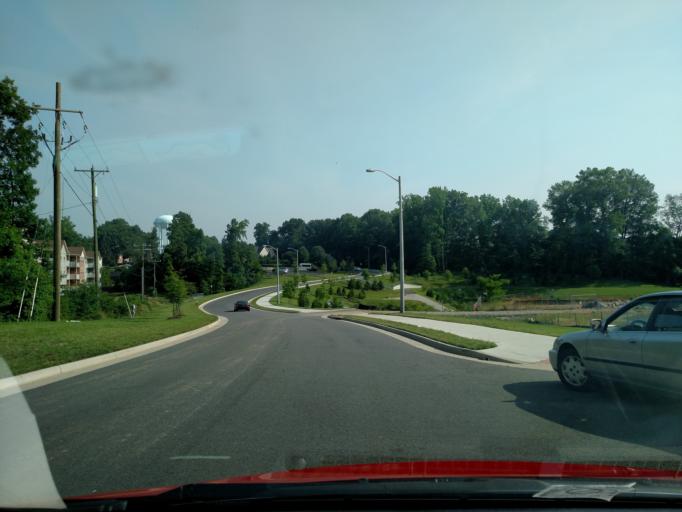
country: US
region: Virginia
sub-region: Fairfax County
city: Merrifield
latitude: 38.8633
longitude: -77.2323
